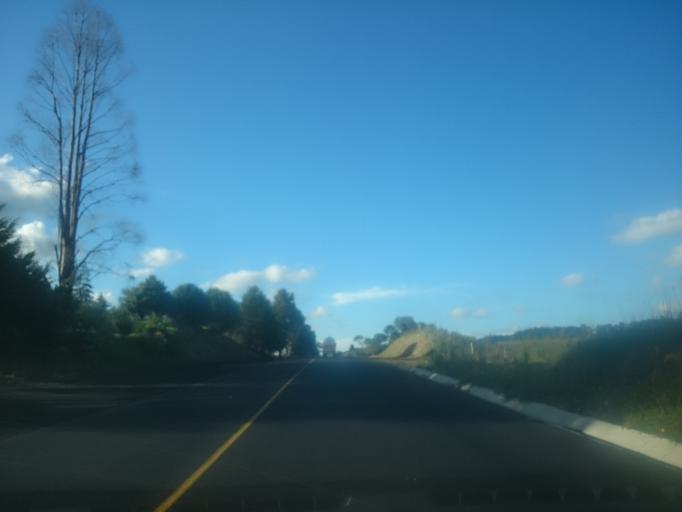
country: BR
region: Santa Catarina
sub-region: Sao Joaquim
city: Sao Joaquim
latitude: -28.0551
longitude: -50.0738
